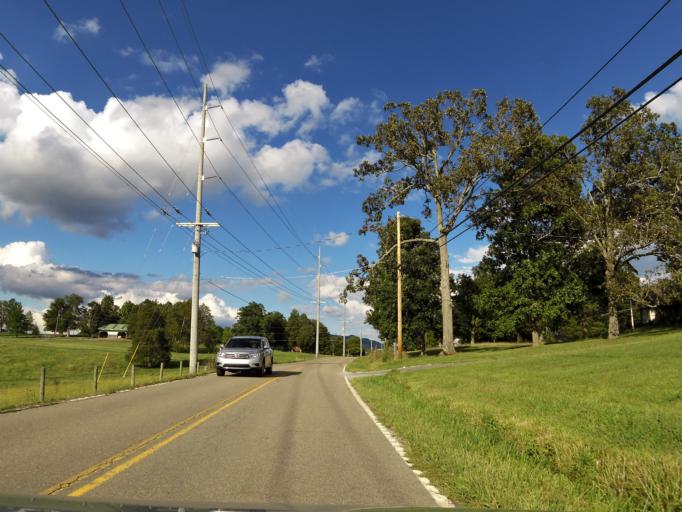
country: US
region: Tennessee
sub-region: Union County
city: Condon
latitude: 36.1322
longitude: -83.7828
